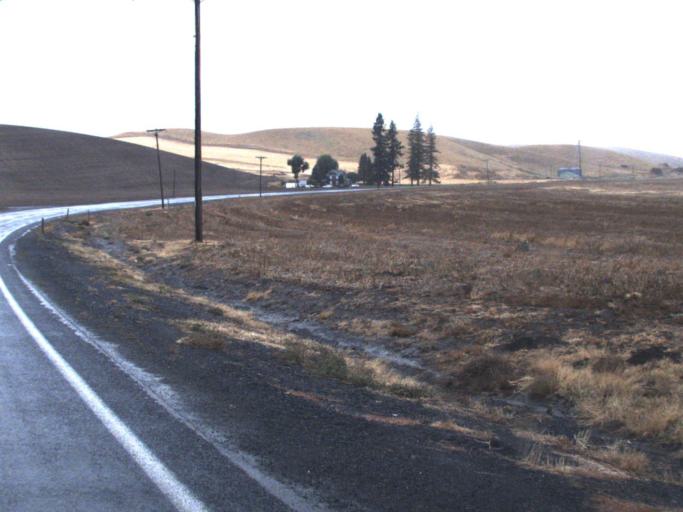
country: US
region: Washington
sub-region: Whitman County
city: Colfax
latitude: 47.0142
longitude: -117.4892
